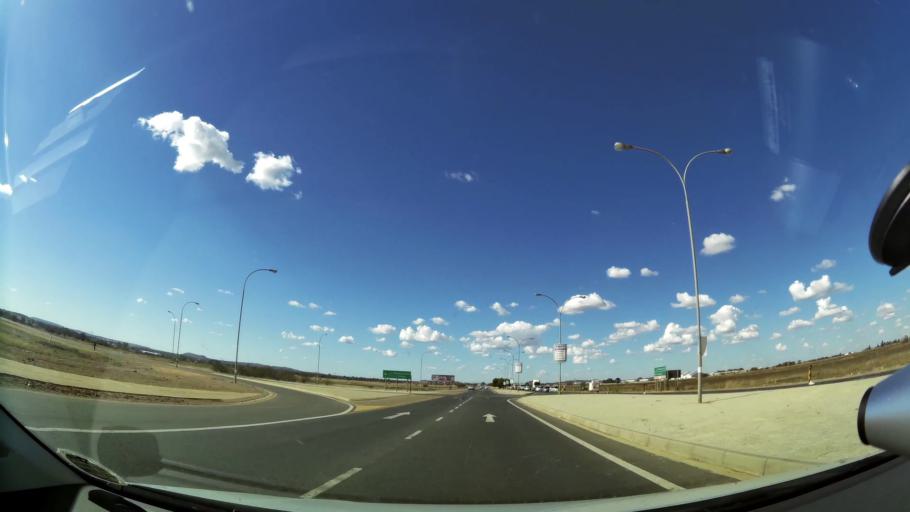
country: ZA
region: North-West
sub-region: Dr Kenneth Kaunda District Municipality
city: Klerksdorp
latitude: -26.8723
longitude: 26.6086
